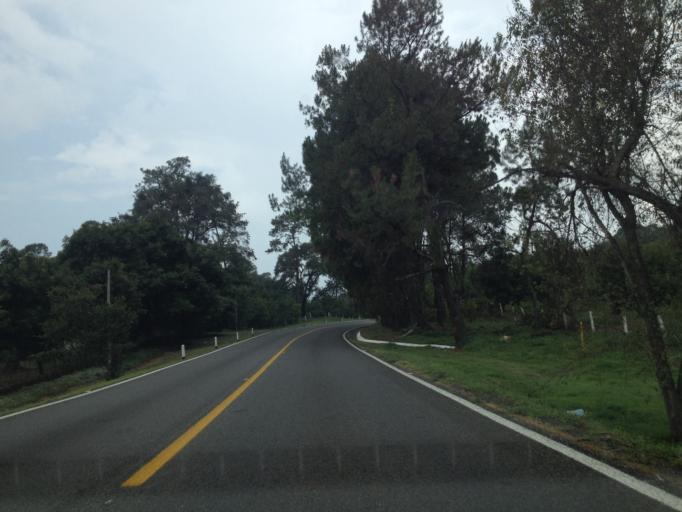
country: MX
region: Michoacan
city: Tingambato
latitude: 19.4761
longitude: -101.9033
